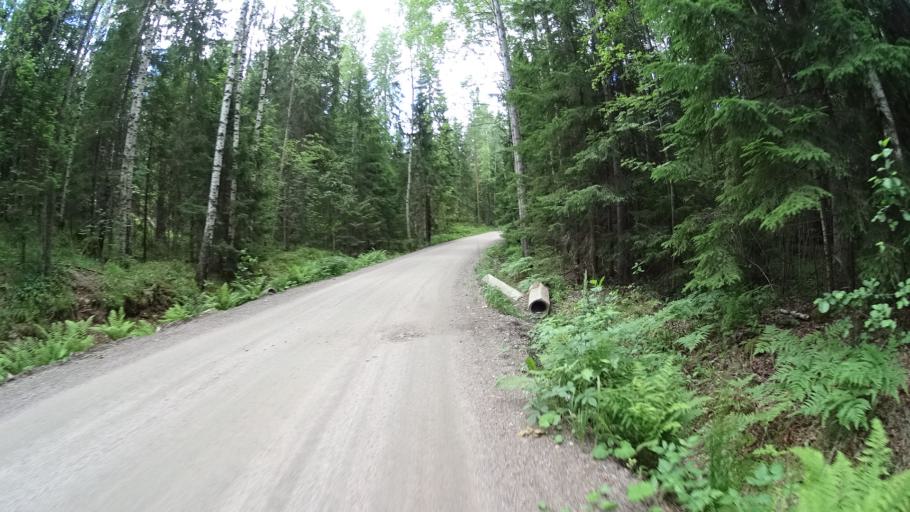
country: FI
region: Uusimaa
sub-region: Helsinki
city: Espoo
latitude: 60.2943
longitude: 24.6186
